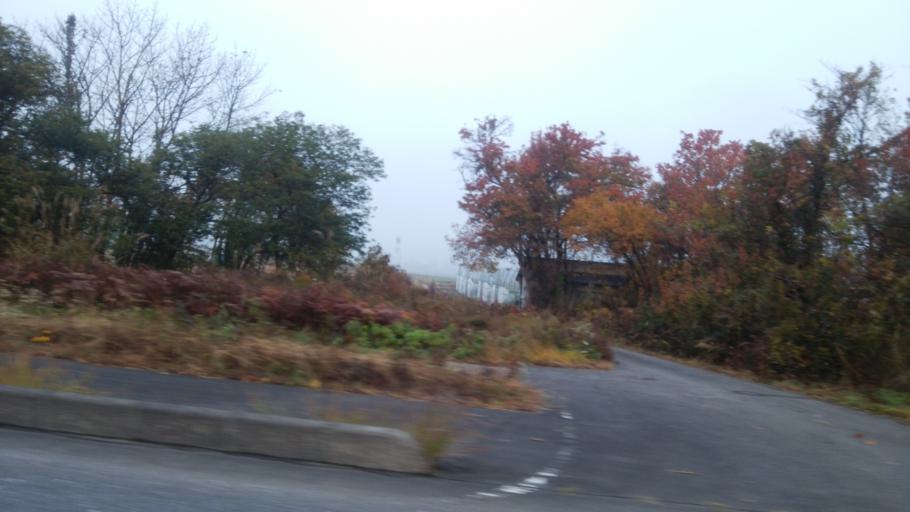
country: JP
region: Fukushima
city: Kitakata
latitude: 37.5550
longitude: 139.7621
